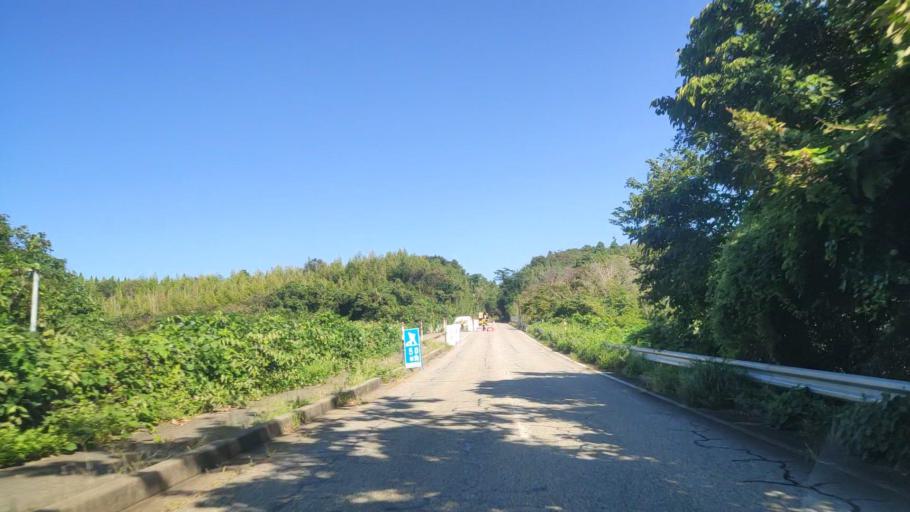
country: JP
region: Ishikawa
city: Hakui
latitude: 37.0863
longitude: 136.7294
